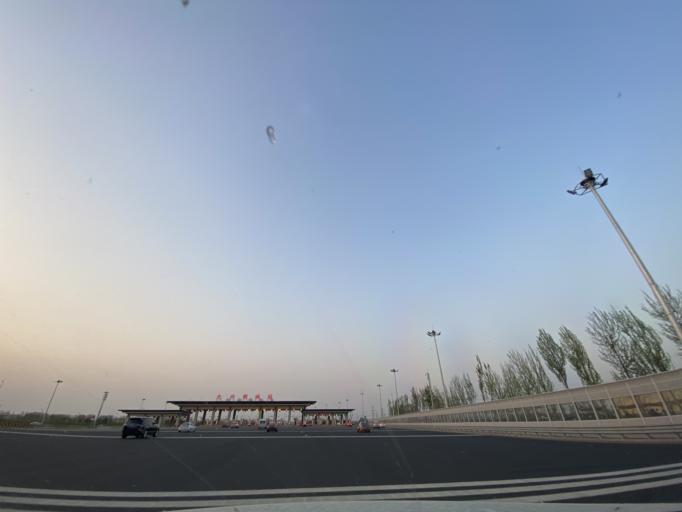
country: CN
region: Beijing
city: Xingfeng
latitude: 39.7258
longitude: 116.3790
